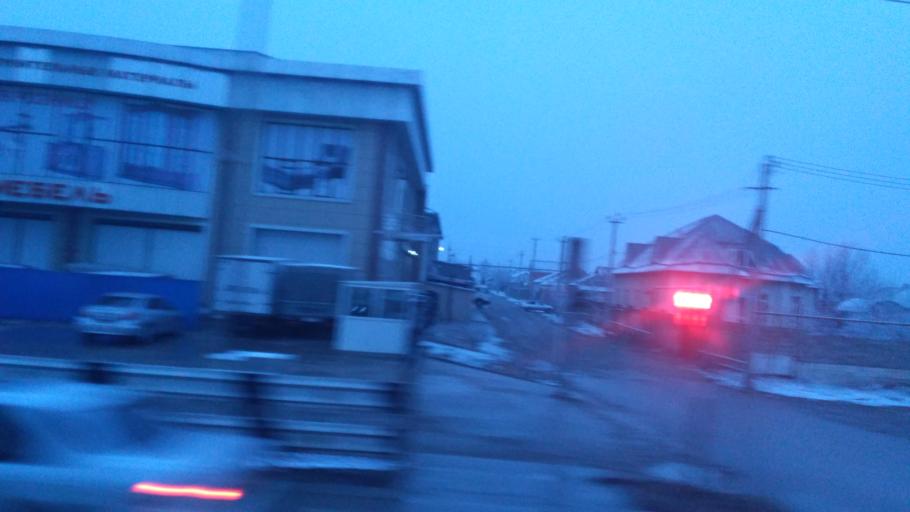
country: KZ
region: Ongtustik Qazaqstan
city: Shymkent
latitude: 42.3653
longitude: 69.5154
